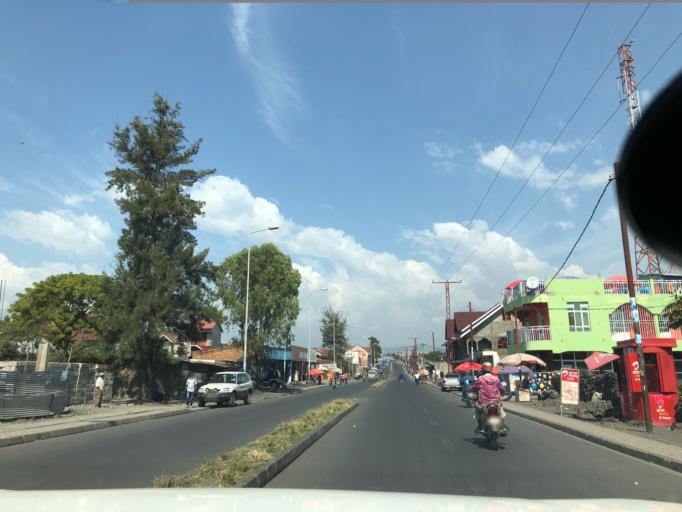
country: CD
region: Nord Kivu
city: Goma
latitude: -1.6582
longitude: 29.1911
